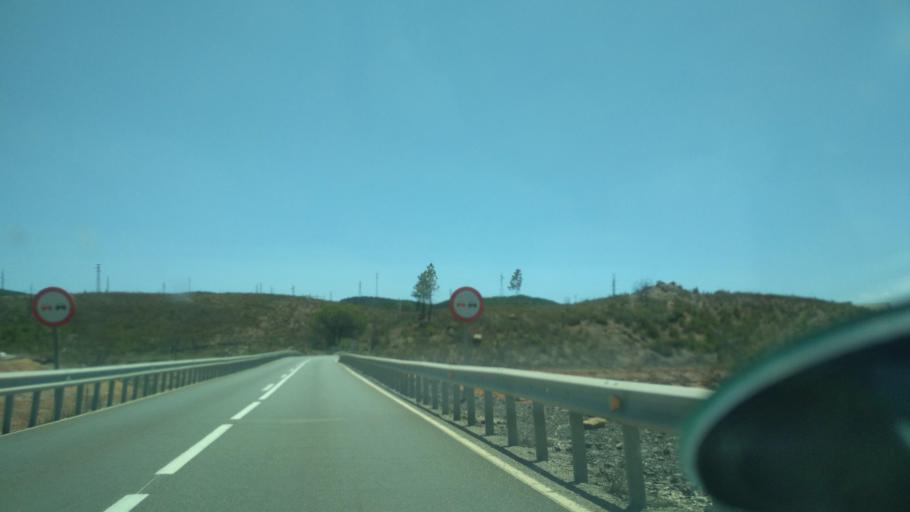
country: ES
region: Andalusia
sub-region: Provincia de Huelva
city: Campofrio
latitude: 37.7299
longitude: -6.5840
